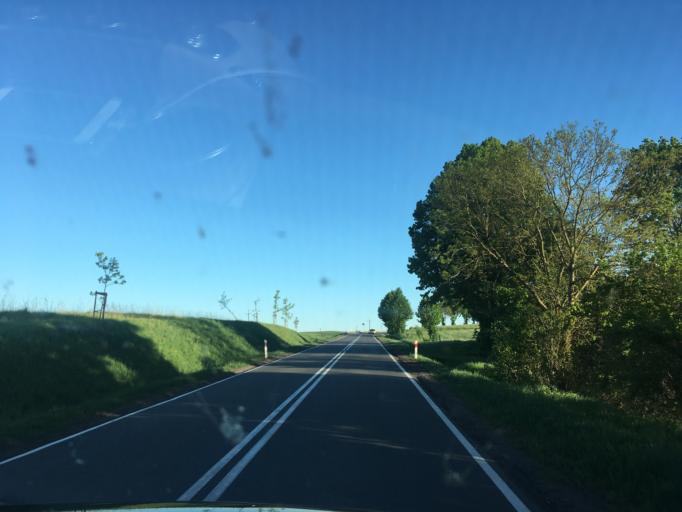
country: PL
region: Warmian-Masurian Voivodeship
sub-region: Powiat mragowski
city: Piecki
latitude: 53.7429
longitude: 21.3352
